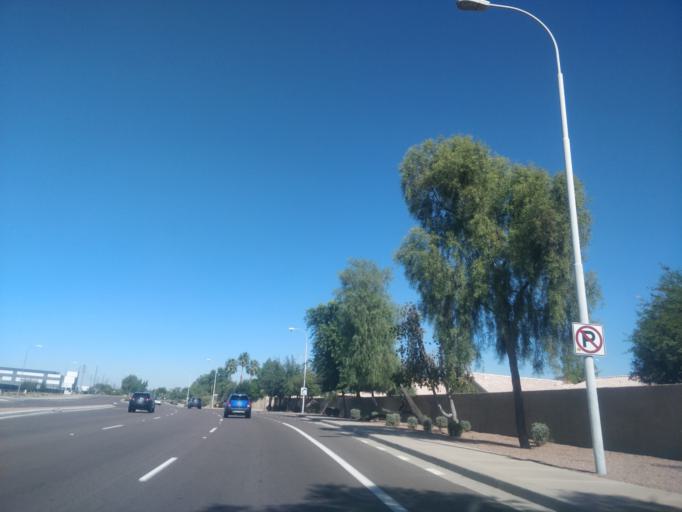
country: US
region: Arizona
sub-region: Maricopa County
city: Sun Lakes
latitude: 33.2642
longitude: -111.8802
